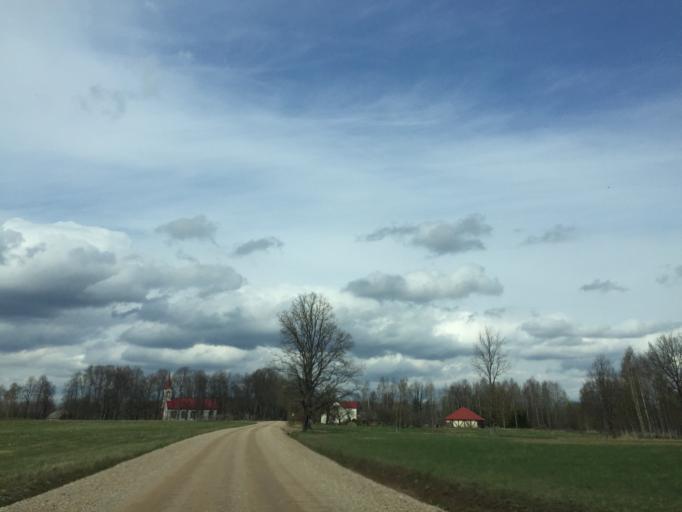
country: LV
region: Ligatne
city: Ligatne
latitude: 57.2142
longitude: 25.0681
